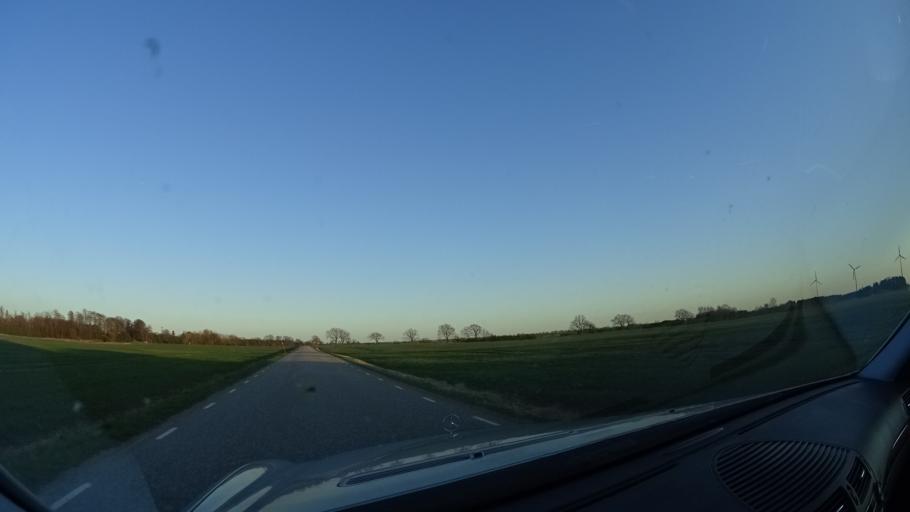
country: SE
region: Skane
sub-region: Hoors Kommun
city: Loberod
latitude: 55.8413
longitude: 13.4540
